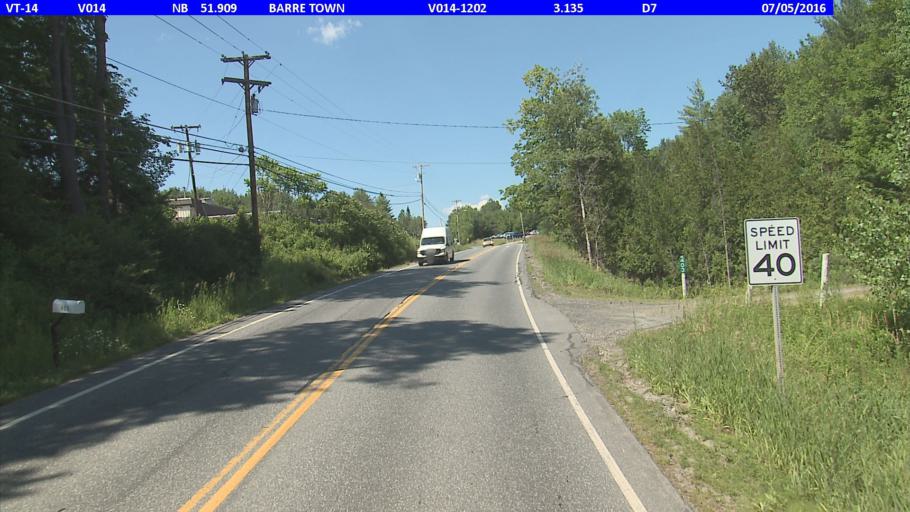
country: US
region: Vermont
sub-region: Washington County
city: Barre
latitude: 44.2233
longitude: -72.4896
